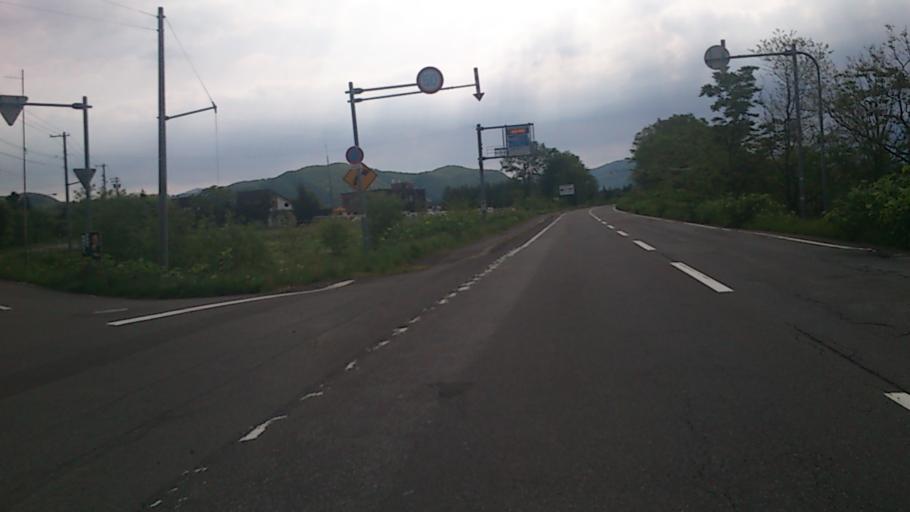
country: JP
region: Hokkaido
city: Kamikawa
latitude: 43.8490
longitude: 142.7444
